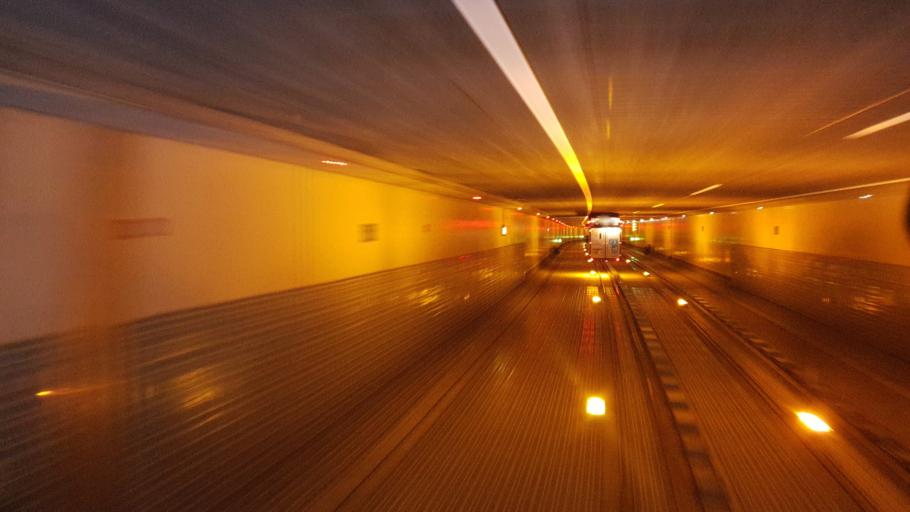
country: AT
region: Carinthia
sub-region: Politischer Bezirk Spittal an der Drau
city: Trebesing
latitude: 46.8866
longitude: 13.5160
